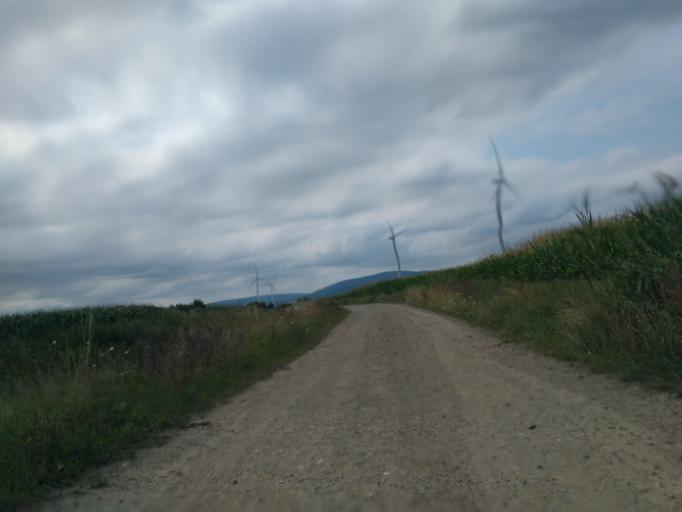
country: PL
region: Subcarpathian Voivodeship
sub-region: Powiat krosnienski
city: Rymanow
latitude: 49.6158
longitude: 21.8472
